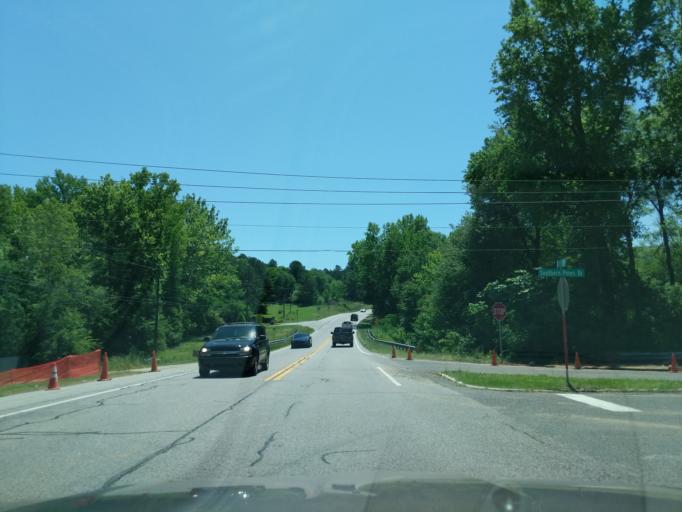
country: US
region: Georgia
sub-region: Columbia County
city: Evans
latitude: 33.5630
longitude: -82.1059
